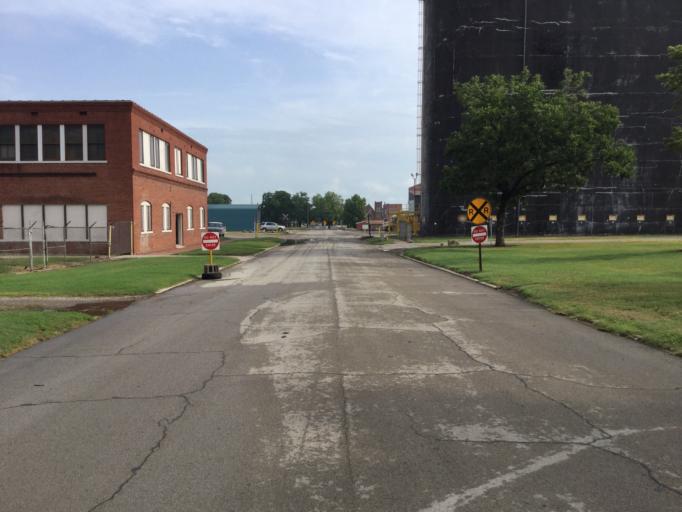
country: US
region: Kansas
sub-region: Montgomery County
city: Coffeyville
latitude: 37.0291
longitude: -95.6178
